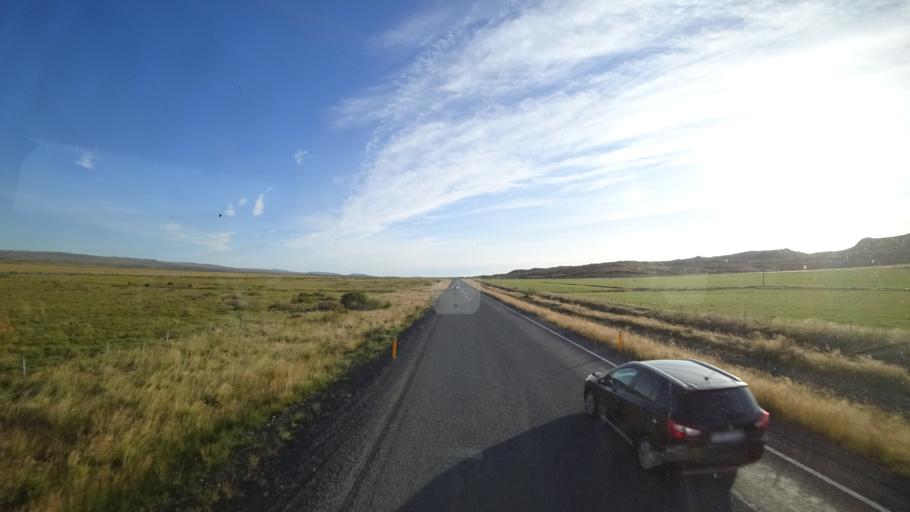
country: IS
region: South
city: Selfoss
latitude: 64.3004
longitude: -20.3311
